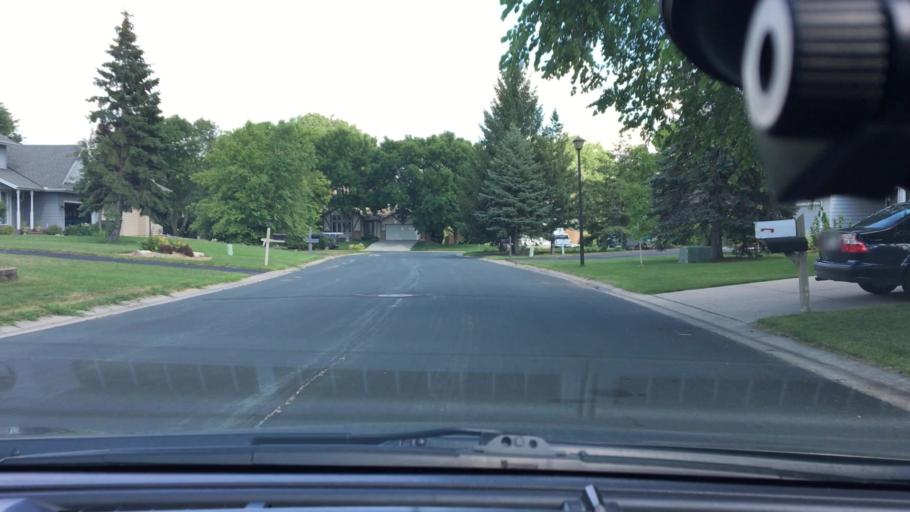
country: US
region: Minnesota
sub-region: Hennepin County
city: New Hope
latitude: 45.0402
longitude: -93.4242
